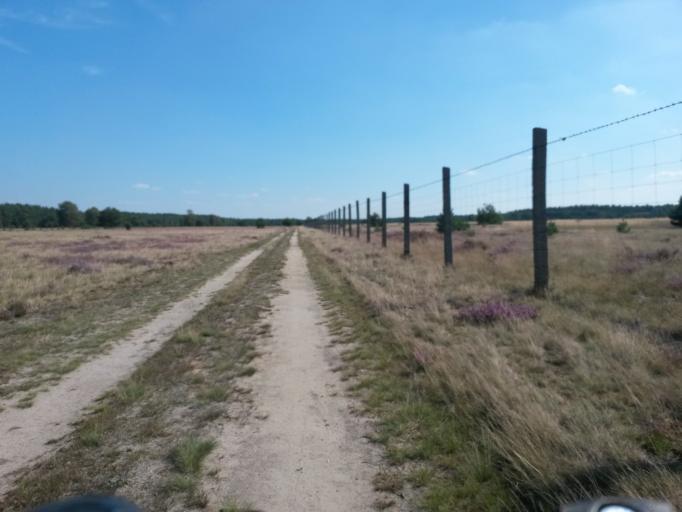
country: DE
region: Brandenburg
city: Templin
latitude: 53.0331
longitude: 13.5611
